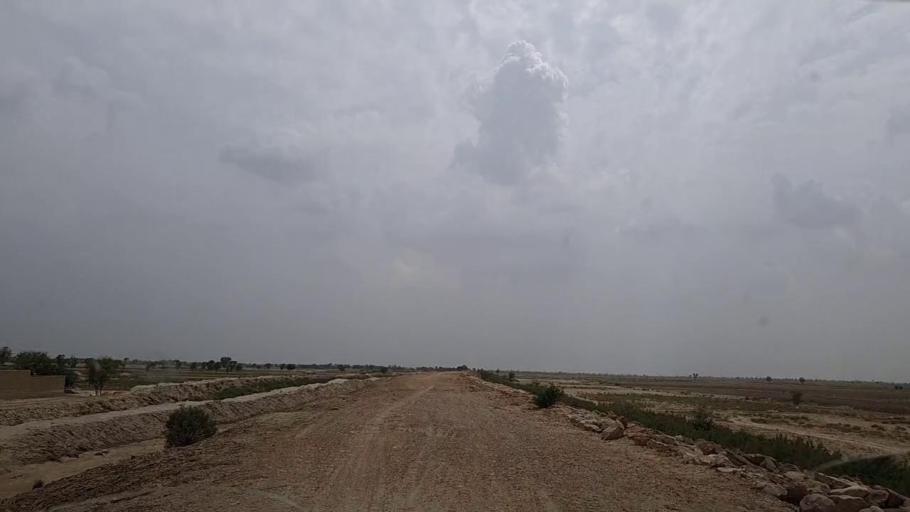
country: PK
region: Sindh
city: Johi
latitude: 26.7471
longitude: 67.5888
